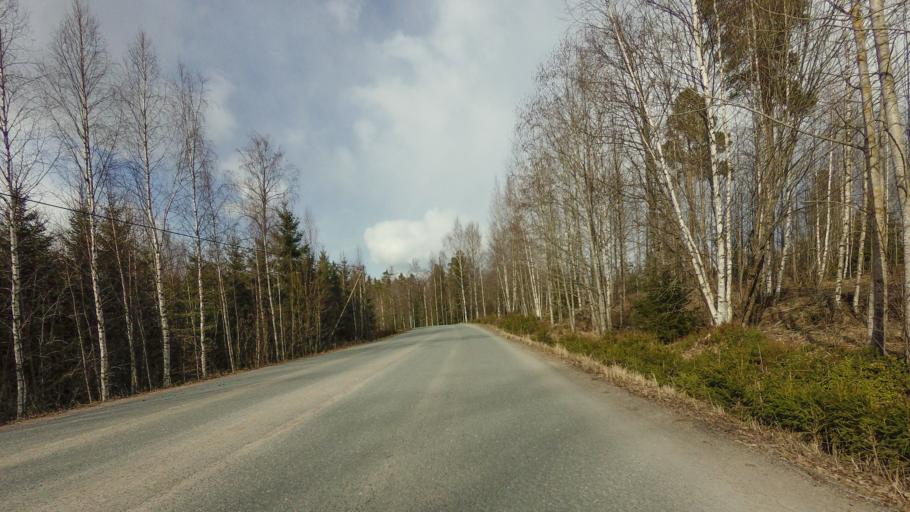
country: FI
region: Varsinais-Suomi
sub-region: Salo
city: Suomusjaervi
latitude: 60.3262
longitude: 23.7047
